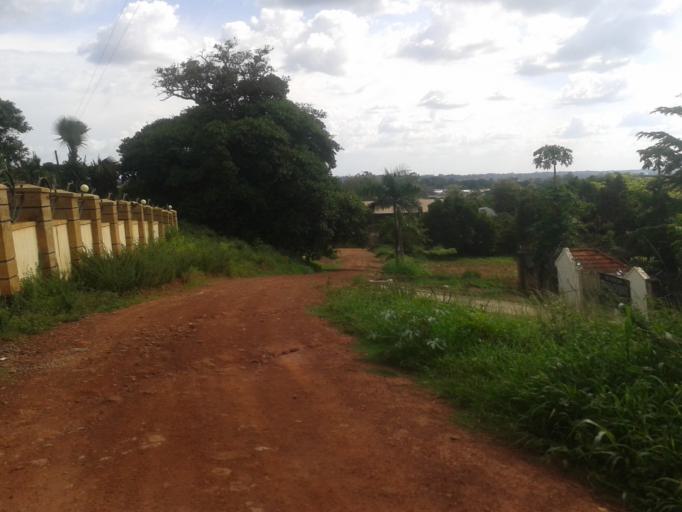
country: UG
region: Northern Region
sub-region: Gulu District
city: Gulu
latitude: 2.7824
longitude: 32.2955
